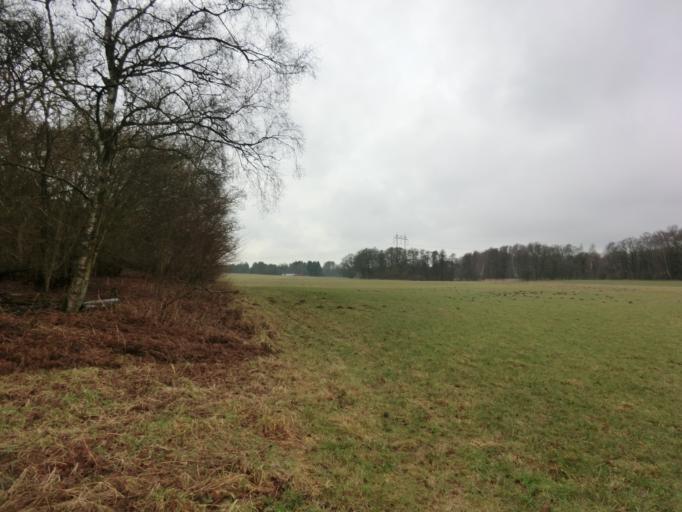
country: SE
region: Skane
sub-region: Hoors Kommun
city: Loberod
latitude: 55.7309
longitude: 13.4019
